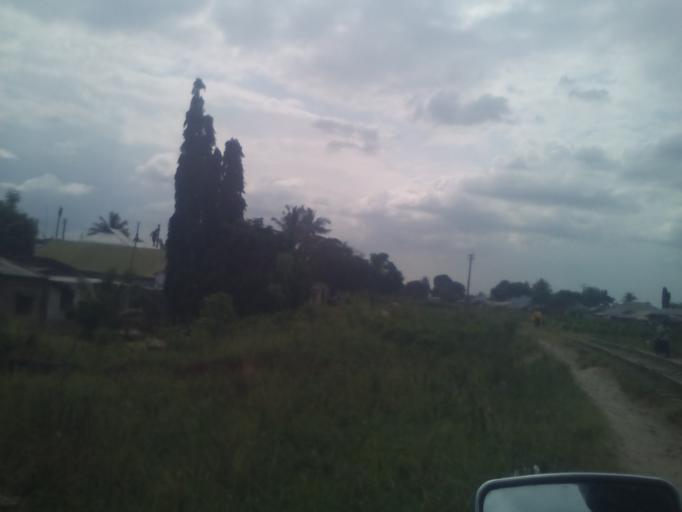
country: TZ
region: Dar es Salaam
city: Dar es Salaam
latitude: -6.8631
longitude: 39.2455
